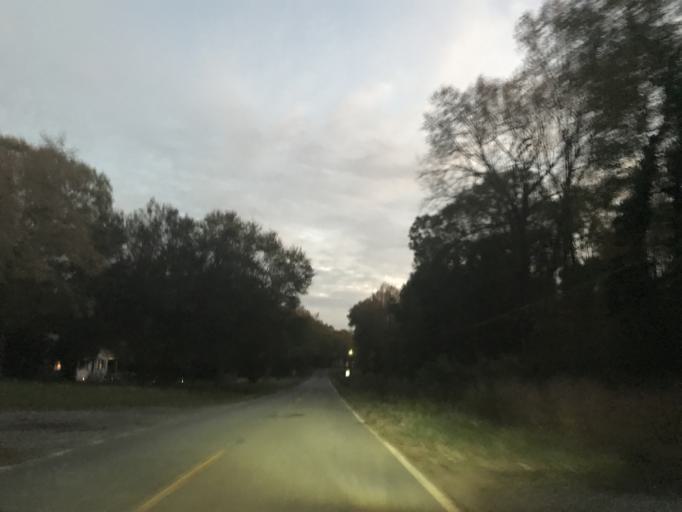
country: US
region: South Carolina
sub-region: Spartanburg County
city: Mayo
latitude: 35.0550
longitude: -81.8912
